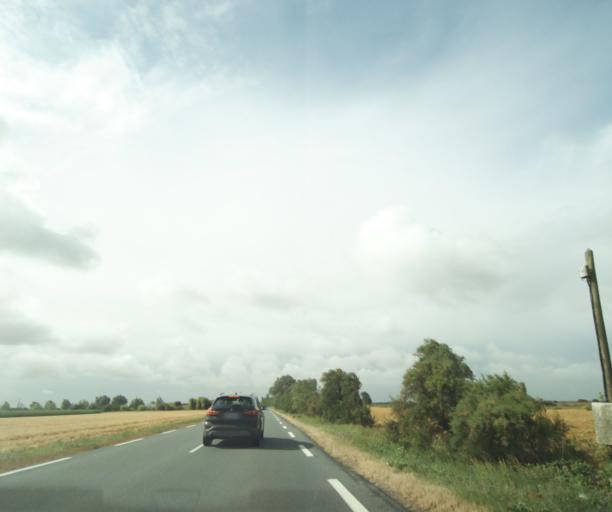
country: FR
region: Poitou-Charentes
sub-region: Departement de la Charente-Maritime
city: Andilly
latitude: 46.2652
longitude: -1.0674
